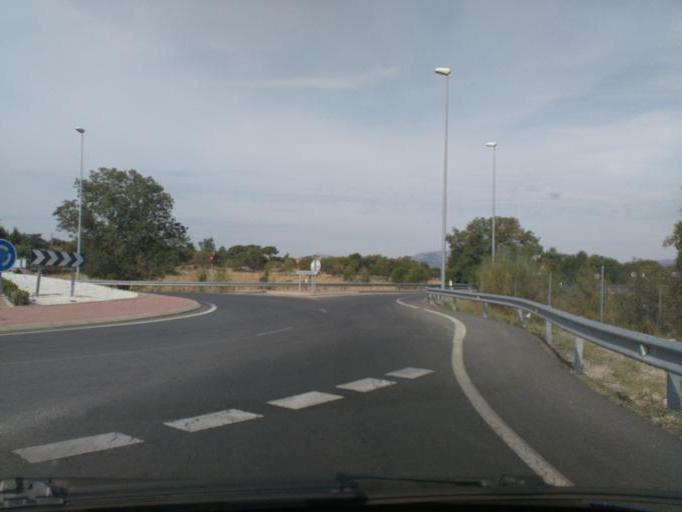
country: ES
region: Madrid
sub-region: Provincia de Madrid
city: Galapagar
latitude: 40.5776
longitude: -3.9895
